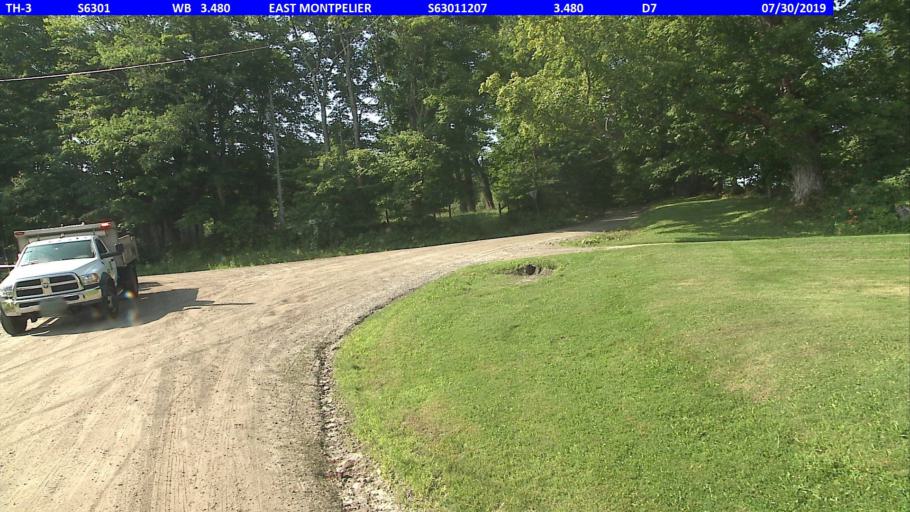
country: US
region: Vermont
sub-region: Washington County
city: Montpelier
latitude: 44.3069
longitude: -72.5107
